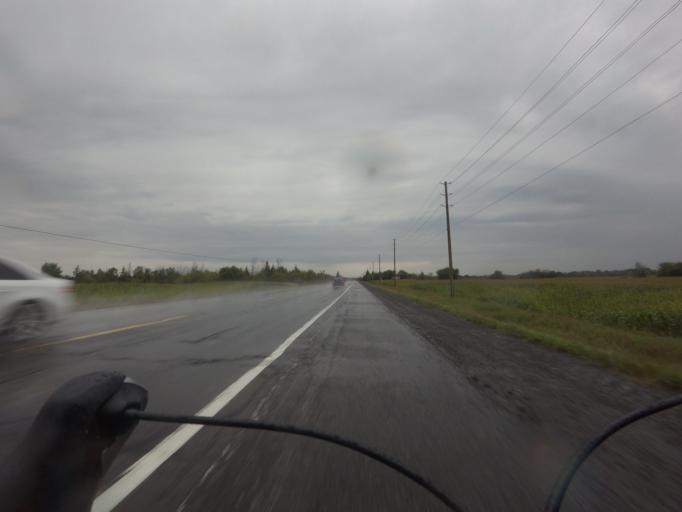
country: CA
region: Ontario
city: Bells Corners
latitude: 45.2322
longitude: -75.7150
